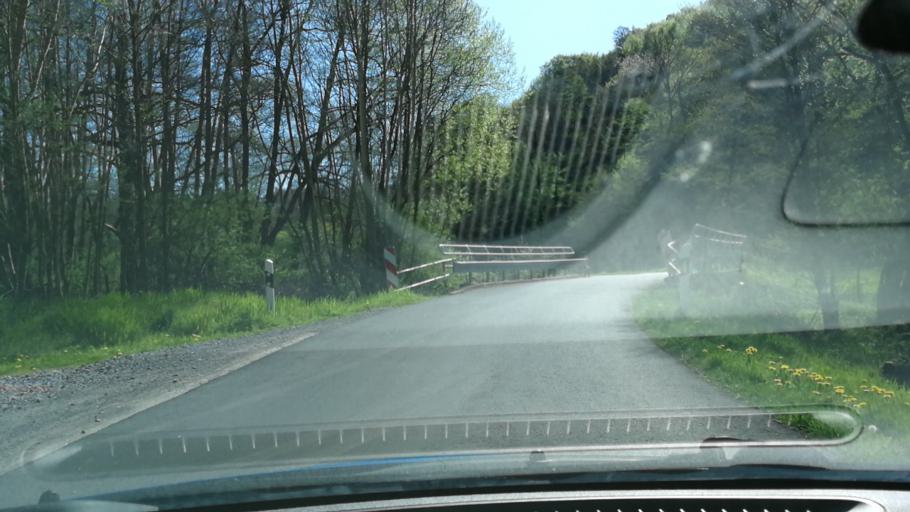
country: DE
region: Lower Saxony
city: Buhren
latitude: 51.5422
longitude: 9.6322
